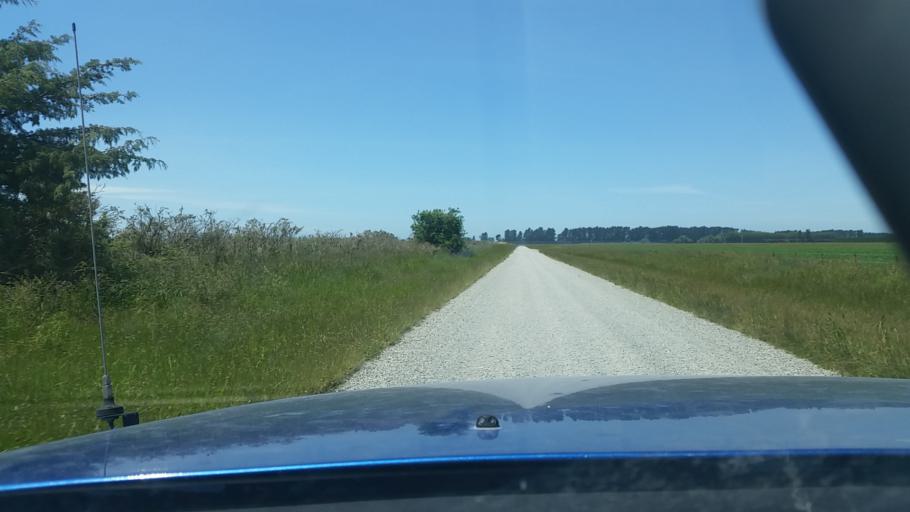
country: NZ
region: Canterbury
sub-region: Ashburton District
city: Tinwald
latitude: -43.9722
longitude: 171.7433
